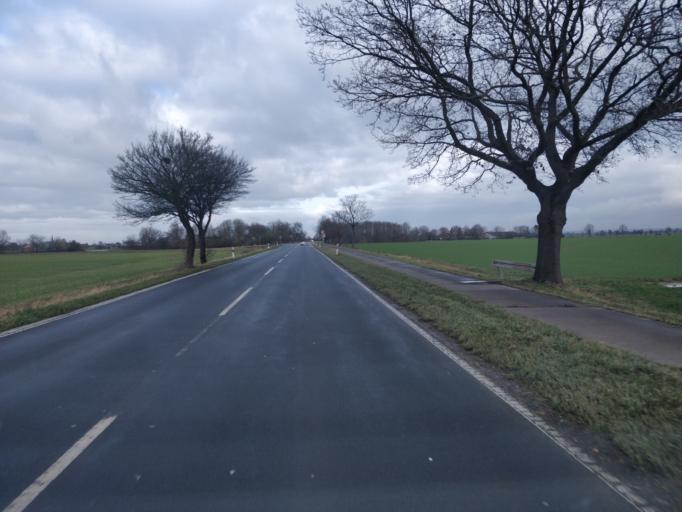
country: DE
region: North Rhine-Westphalia
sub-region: Regierungsbezirk Koln
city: Euskirchen
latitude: 50.6382
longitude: 6.8423
